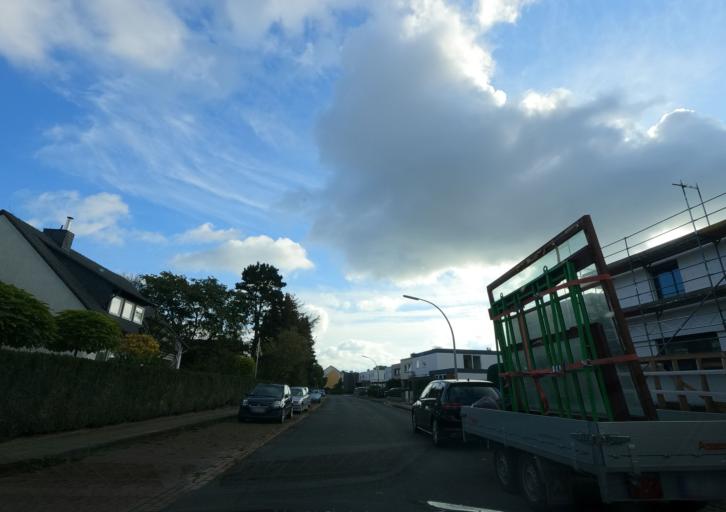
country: DE
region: Lower Saxony
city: Leiferde
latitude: 52.2391
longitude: 10.4836
